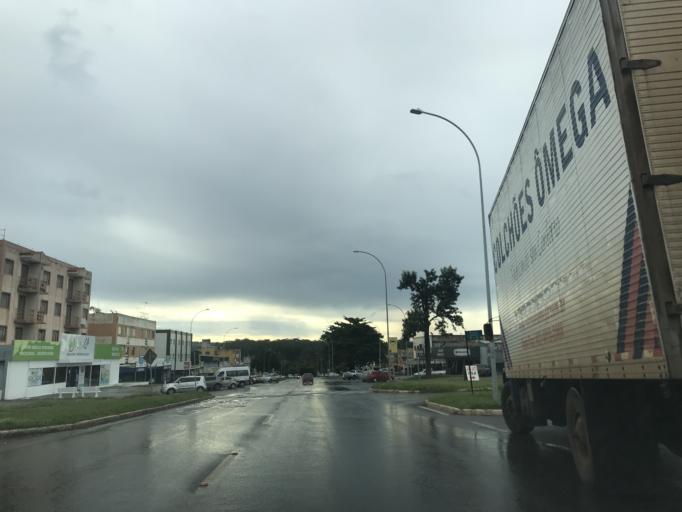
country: BR
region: Federal District
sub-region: Brasilia
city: Brasilia
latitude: -15.6425
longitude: -47.8054
